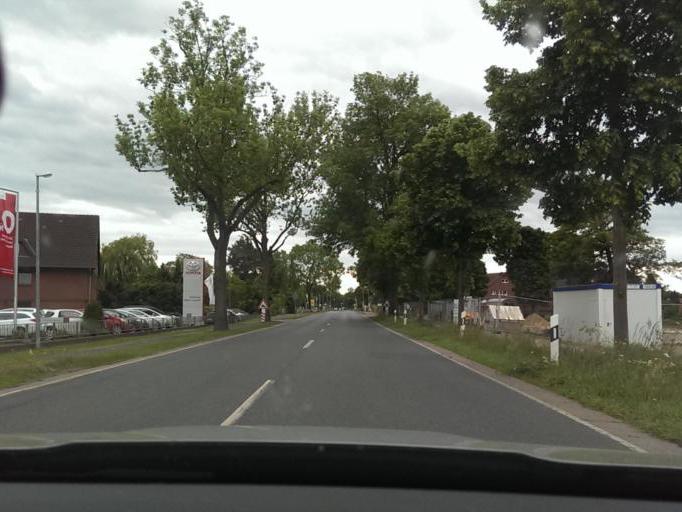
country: DE
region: Lower Saxony
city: Elze
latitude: 52.5821
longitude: 9.7288
